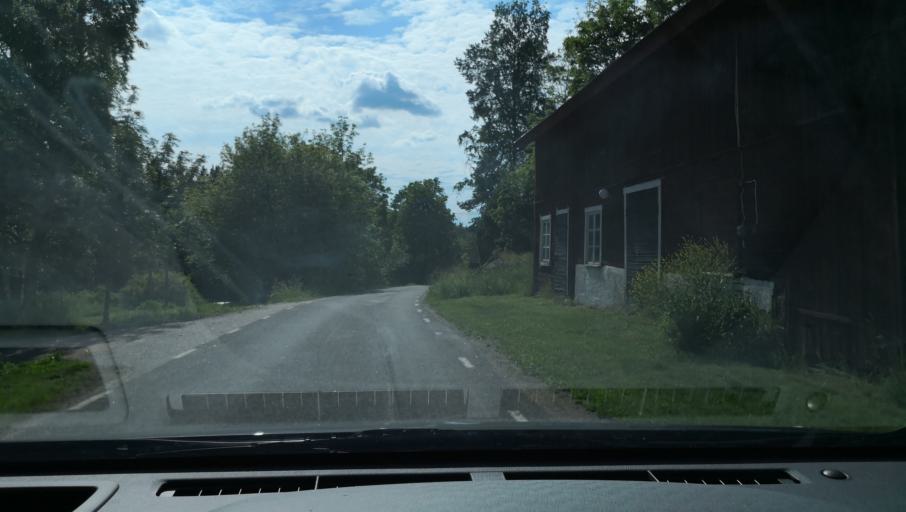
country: SE
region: Uppsala
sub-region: Enkopings Kommun
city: Orsundsbro
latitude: 59.8415
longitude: 17.1981
